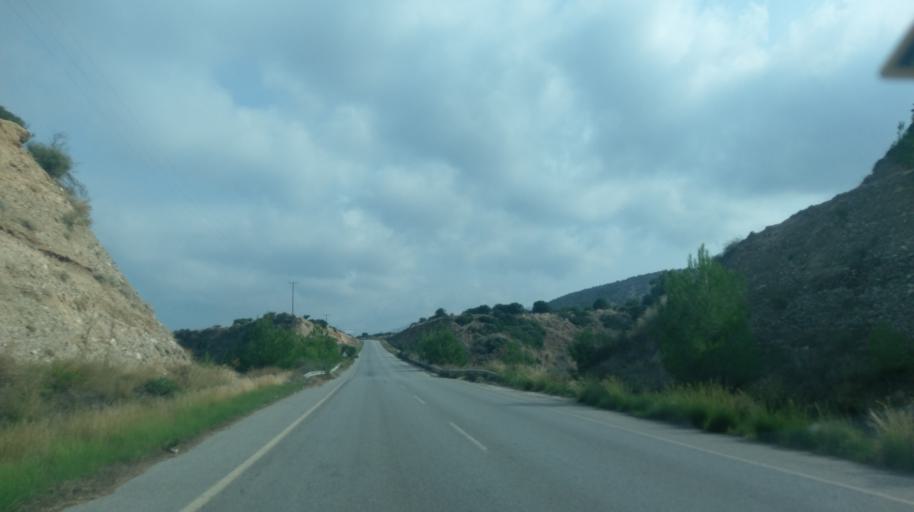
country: CY
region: Ammochostos
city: Lefkonoiko
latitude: 35.3538
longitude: 33.6462
